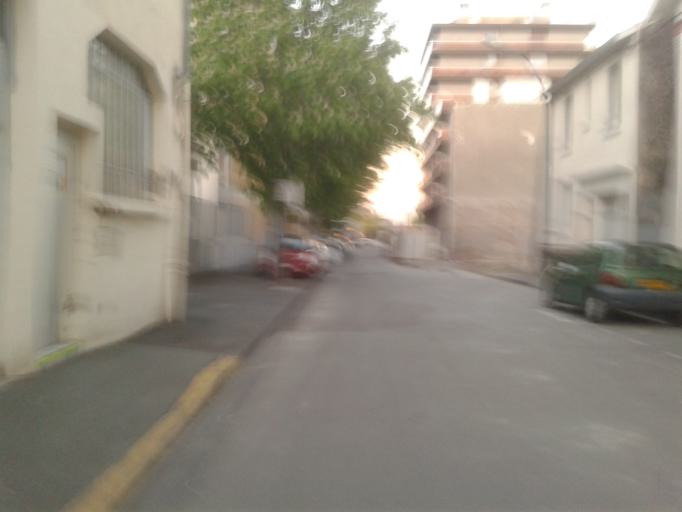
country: FR
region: Auvergne
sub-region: Departement du Puy-de-Dome
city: Clermont-Ferrand
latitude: 45.7694
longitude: 3.0817
